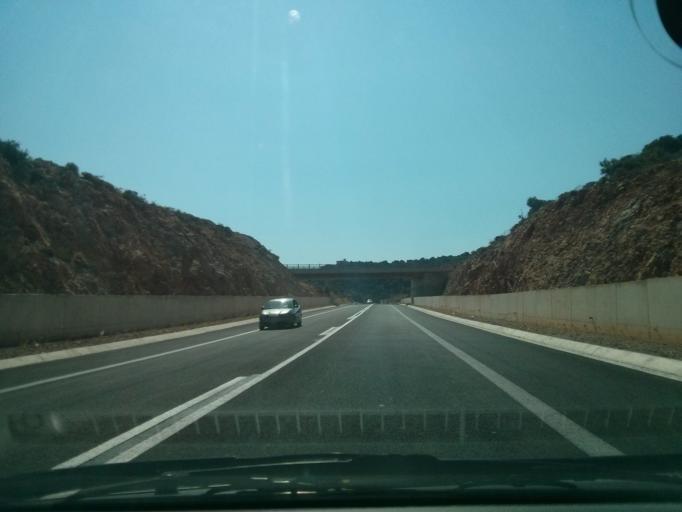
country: GR
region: Crete
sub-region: Nomos Lasithiou
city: Agios Nikolaos
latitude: 35.1653
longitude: 25.7040
